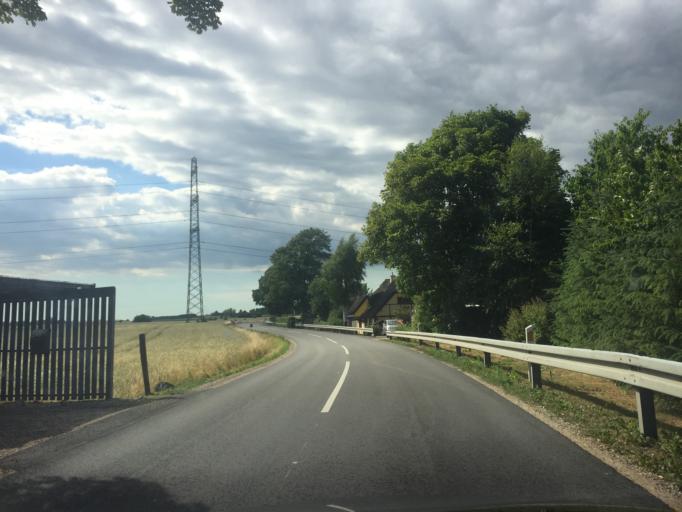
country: DK
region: Capital Region
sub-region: Egedal Kommune
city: Vekso
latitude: 55.7064
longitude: 12.2246
